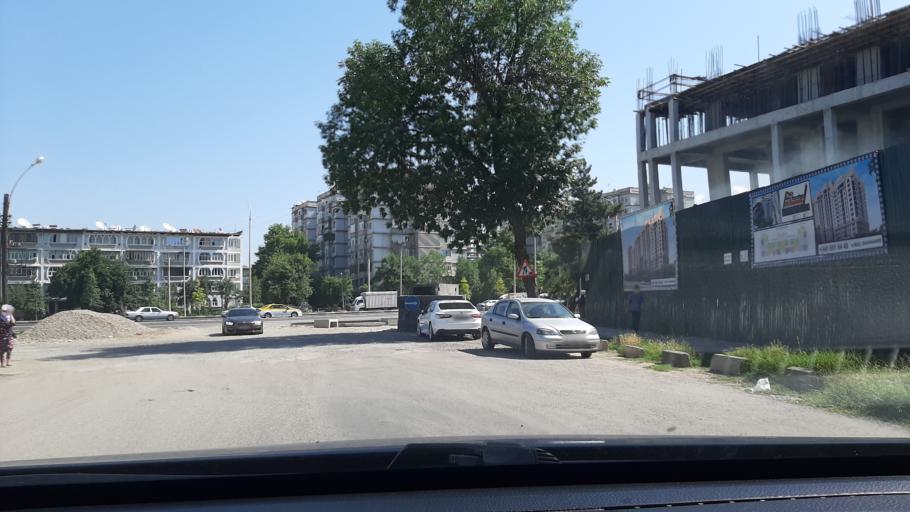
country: TJ
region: Dushanbe
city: Dushanbe
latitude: 38.5577
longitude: 68.7576
